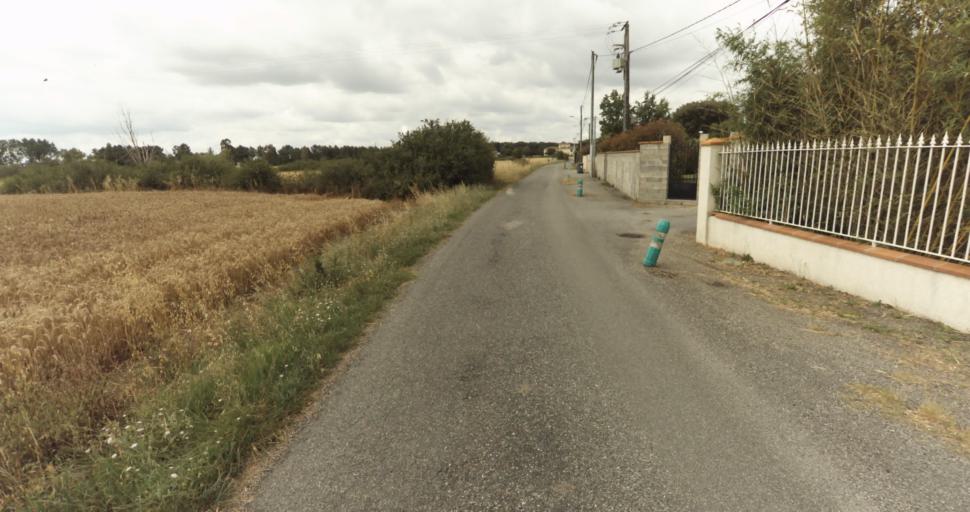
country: FR
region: Midi-Pyrenees
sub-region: Departement de la Haute-Garonne
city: Fonsorbes
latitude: 43.5475
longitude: 1.2161
